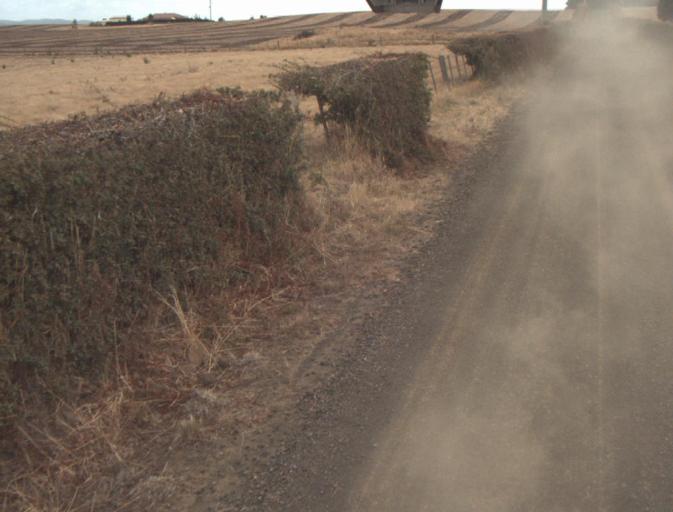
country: AU
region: Tasmania
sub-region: Northern Midlands
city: Evandale
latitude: -41.5242
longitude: 147.2658
